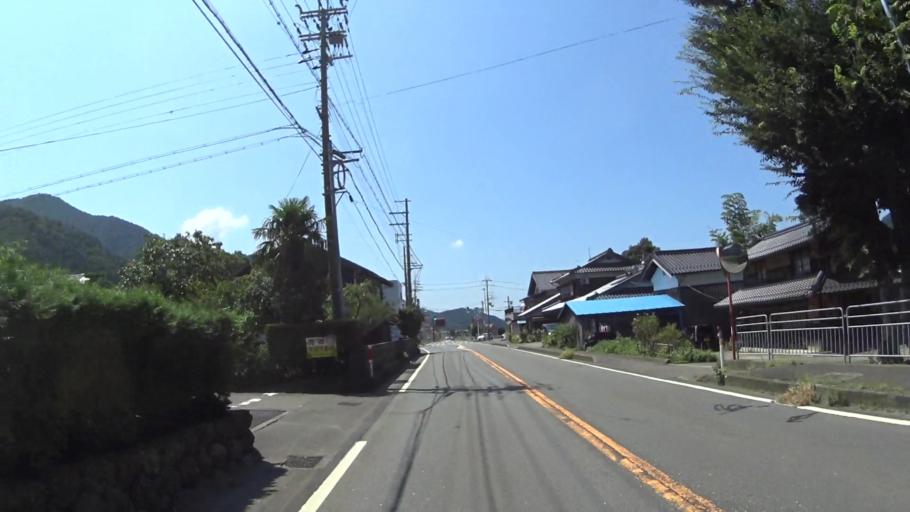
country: JP
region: Fukui
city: Obama
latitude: 35.4635
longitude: 135.8539
